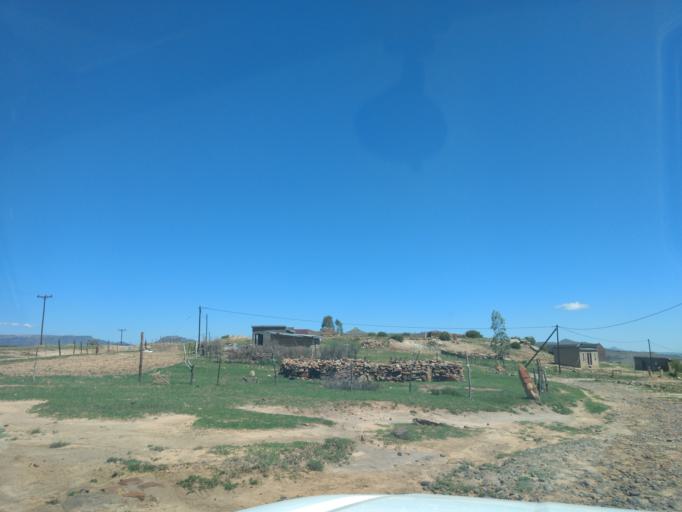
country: LS
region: Maseru
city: Maseru
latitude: -29.4605
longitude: 27.3733
